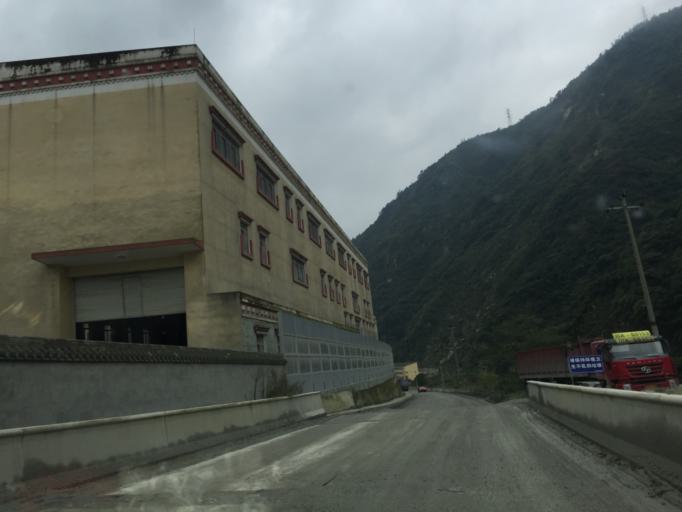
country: CN
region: Sichuan
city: Guangsheng
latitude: 31.0797
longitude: 103.4847
